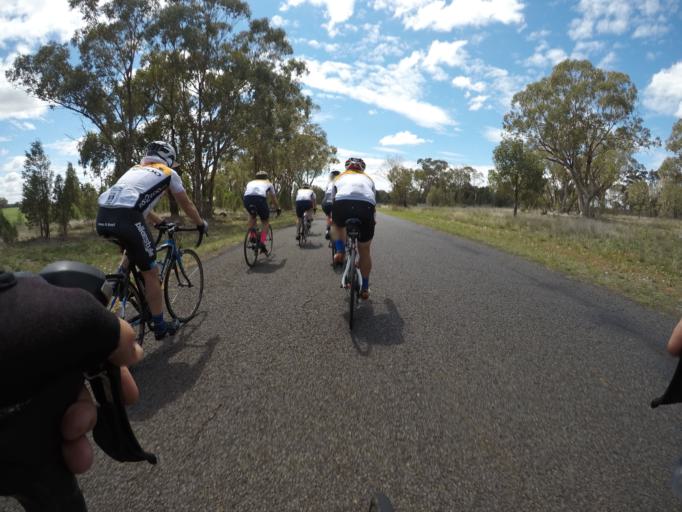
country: AU
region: New South Wales
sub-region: Dubbo Municipality
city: Dubbo
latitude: -32.3663
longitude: 148.5835
